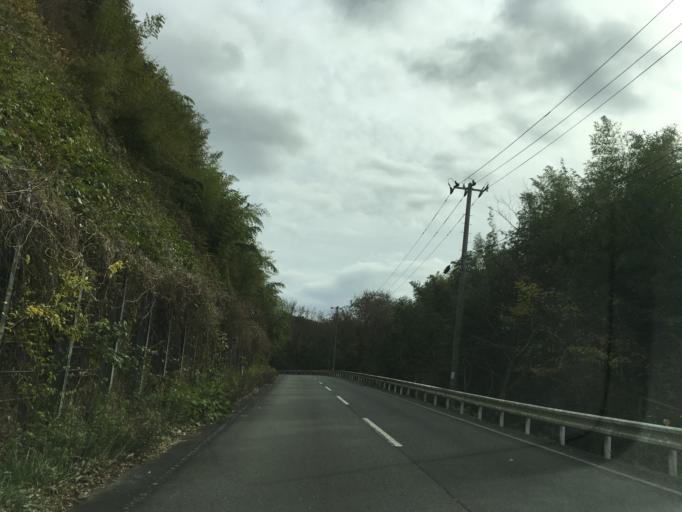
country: JP
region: Iwate
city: Ichinoseki
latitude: 38.7900
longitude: 141.2608
